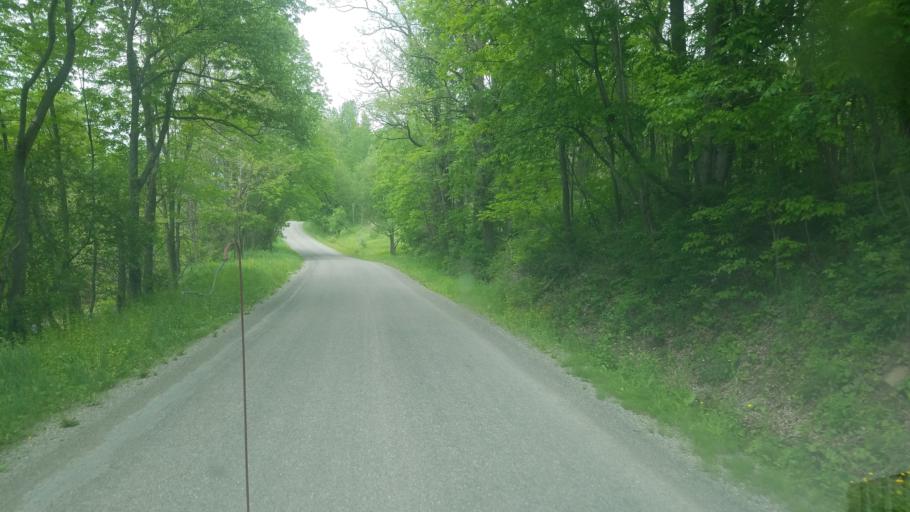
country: US
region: Pennsylvania
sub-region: Tioga County
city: Westfield
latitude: 41.8904
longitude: -77.5998
